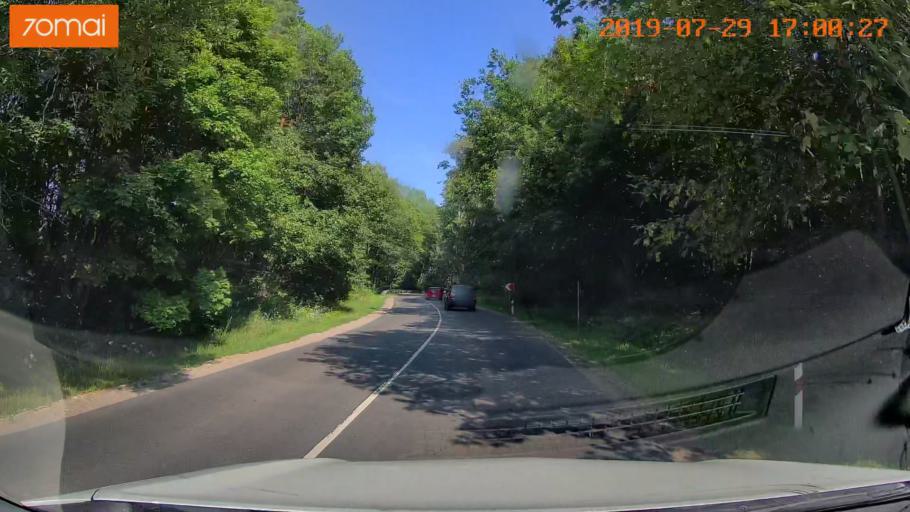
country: RU
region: Kaliningrad
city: Volochayevskoye
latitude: 54.8191
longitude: 20.2260
